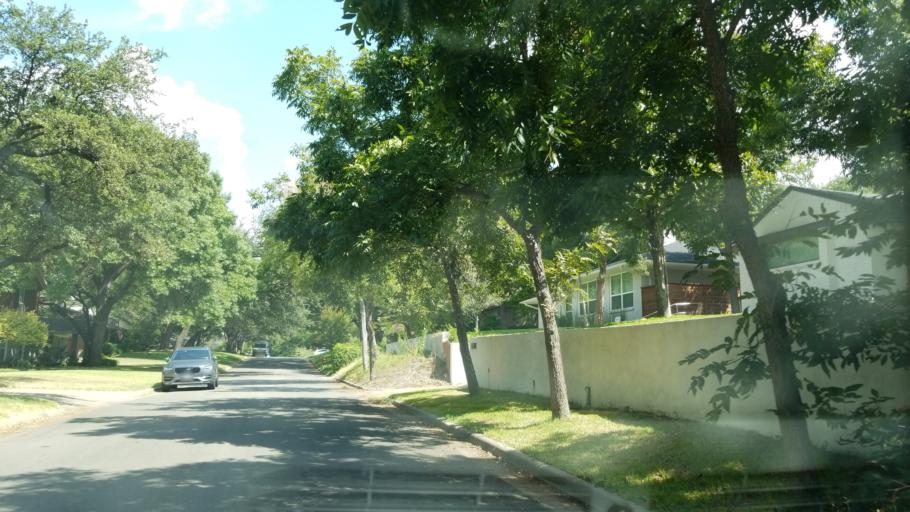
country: US
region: Texas
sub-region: Dallas County
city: Dallas
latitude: 32.7630
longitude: -96.8381
